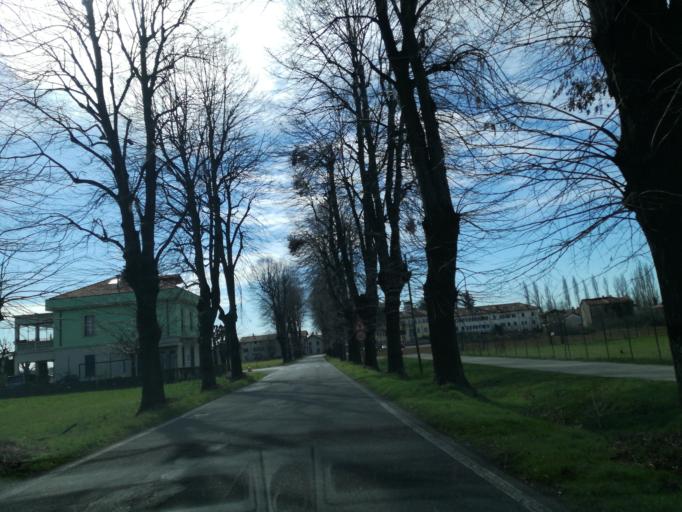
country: IT
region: Lombardy
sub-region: Provincia di Monza e Brianza
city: Villasanta
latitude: 45.6235
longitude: 9.3032
